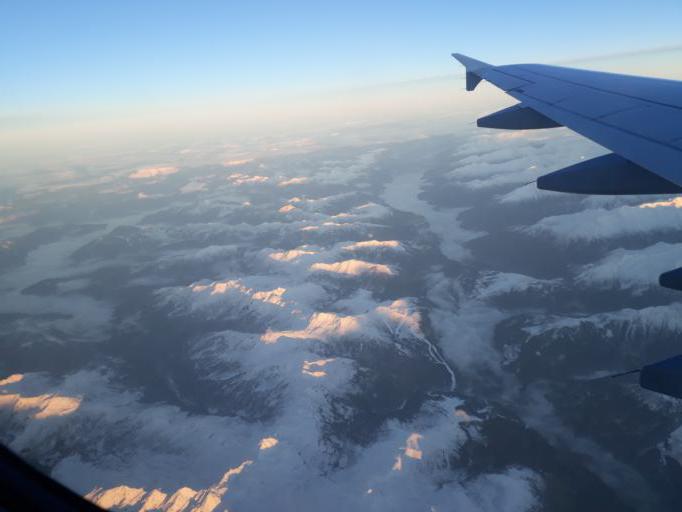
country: AT
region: Tyrol
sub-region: Politischer Bezirk Schwaz
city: Rohrberg
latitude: 47.2385
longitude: 11.9011
